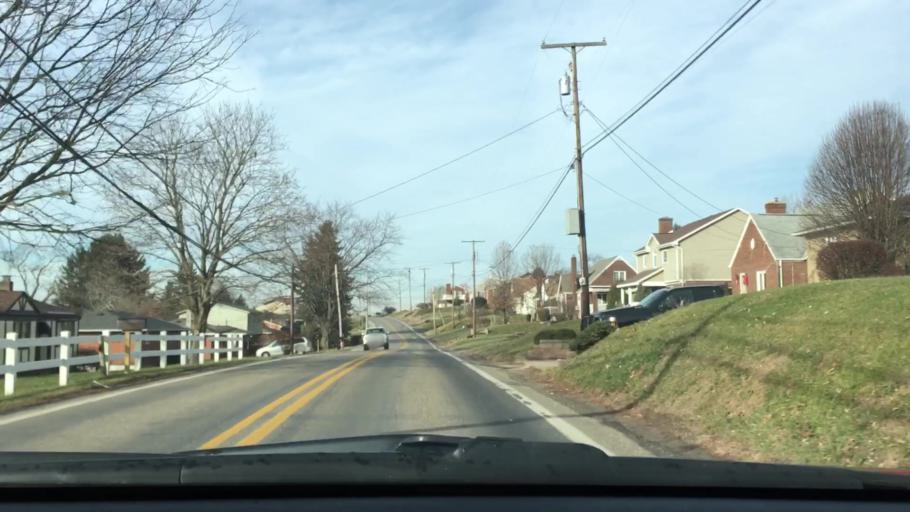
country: US
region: Pennsylvania
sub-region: Allegheny County
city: Jefferson Hills
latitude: 40.2798
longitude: -79.9117
